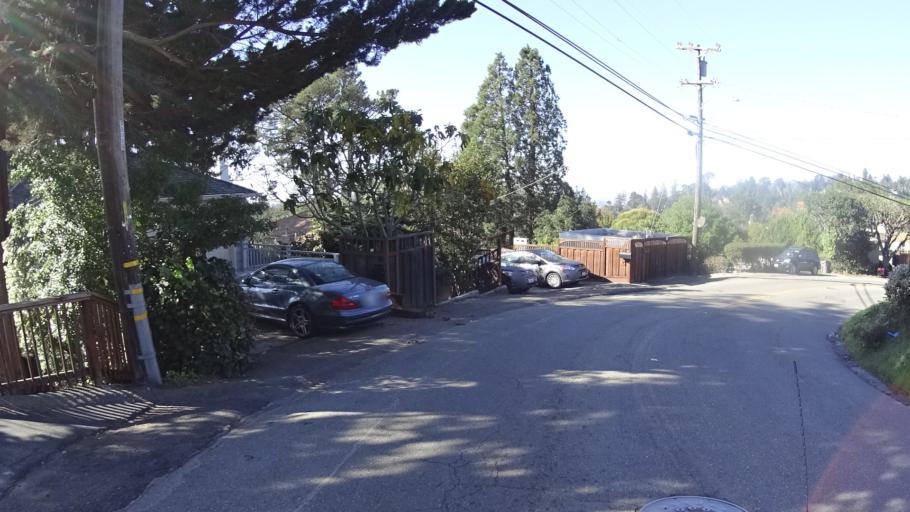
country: US
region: California
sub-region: Alameda County
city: Piedmont
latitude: 37.8322
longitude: -122.2100
